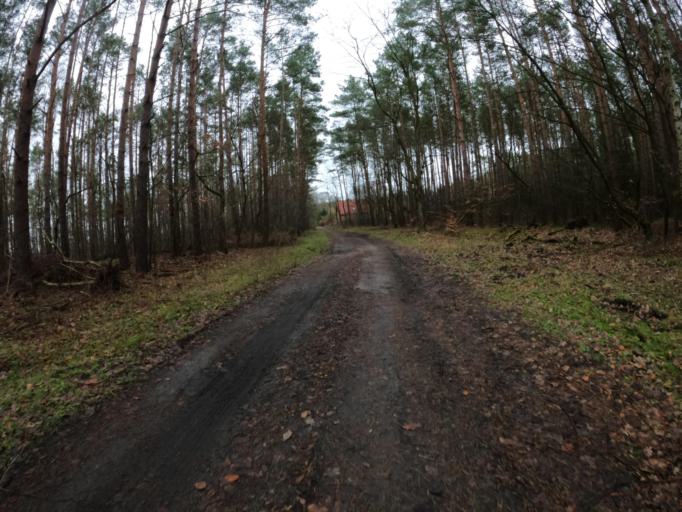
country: PL
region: West Pomeranian Voivodeship
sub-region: Powiat mysliborski
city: Debno
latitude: 52.7402
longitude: 14.7676
